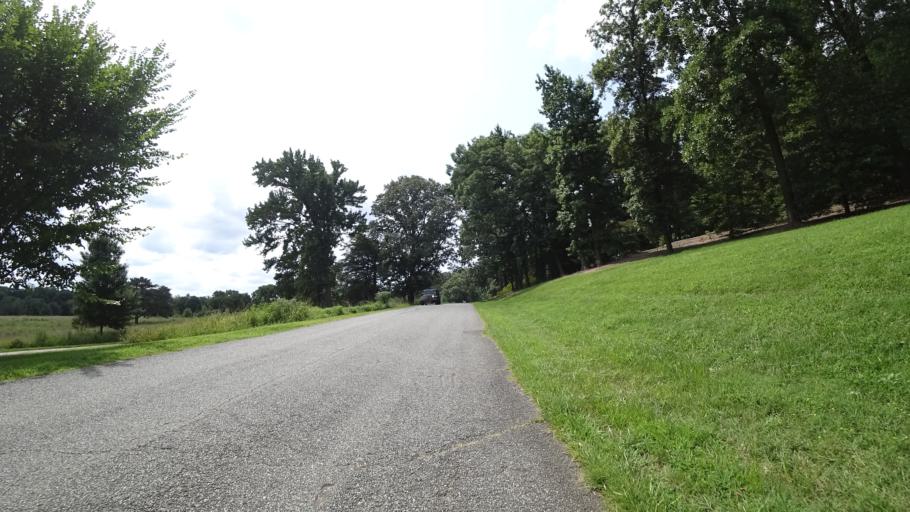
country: US
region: Maryland
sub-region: Prince George's County
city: Mount Rainier
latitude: 38.9097
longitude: -76.9704
